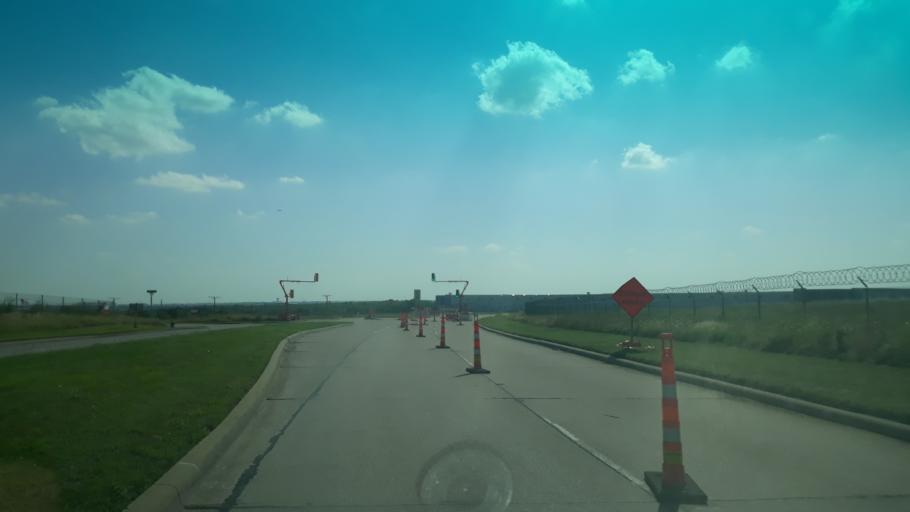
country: US
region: Texas
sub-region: Tarrant County
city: Euless
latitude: 32.8702
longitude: -97.0082
